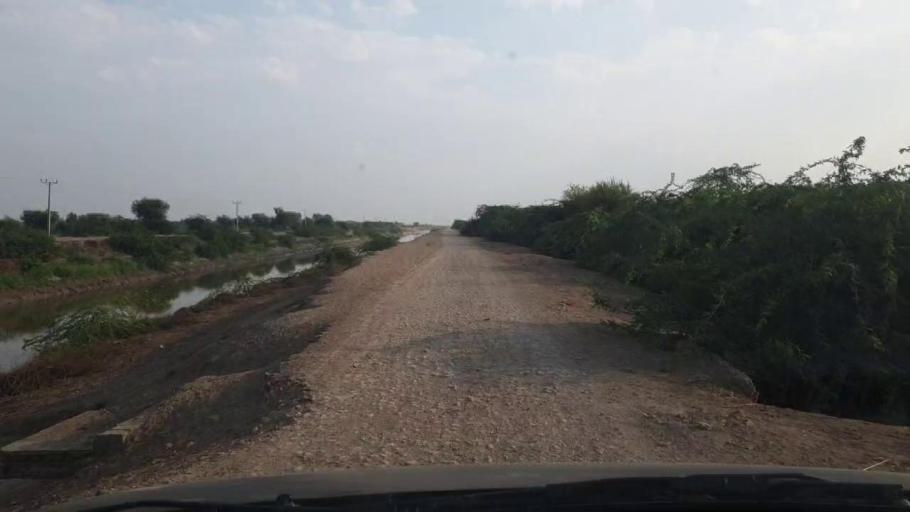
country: PK
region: Sindh
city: Badin
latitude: 24.5184
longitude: 68.6832
